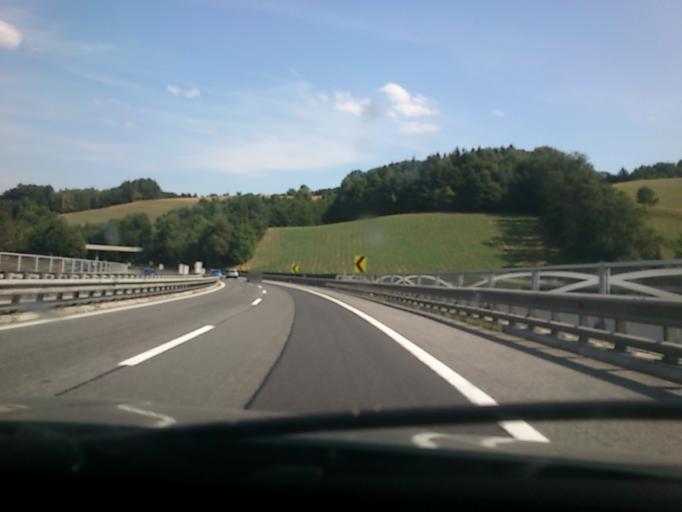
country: AT
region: Lower Austria
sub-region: Politischer Bezirk Neunkirchen
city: Grimmenstein
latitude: 47.6038
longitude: 16.1296
